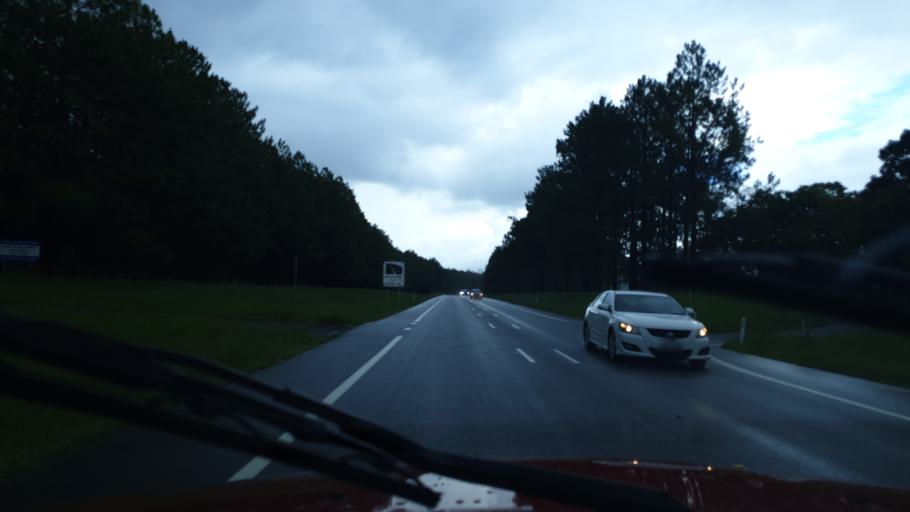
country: AU
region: Queensland
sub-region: Moreton Bay
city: Caboolture
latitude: -26.9792
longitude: 152.9668
